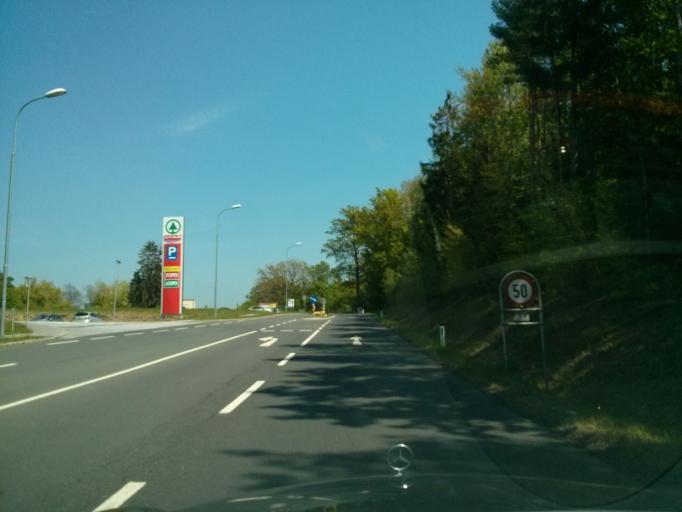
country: AT
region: Burgenland
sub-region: Politischer Bezirk Oberwart
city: Bad Tatzmannsdorf
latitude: 47.3349
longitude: 16.2203
